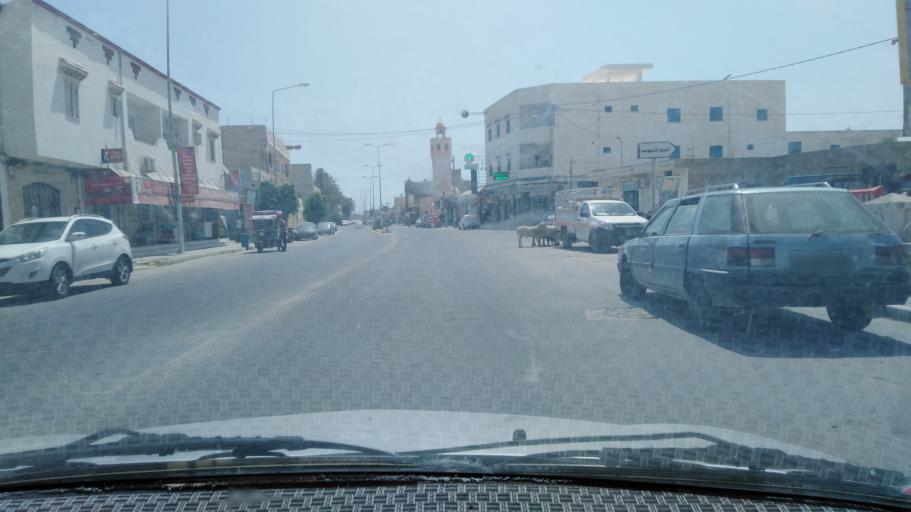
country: TN
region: Qabis
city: Gabes
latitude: 33.9590
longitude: 10.0015
